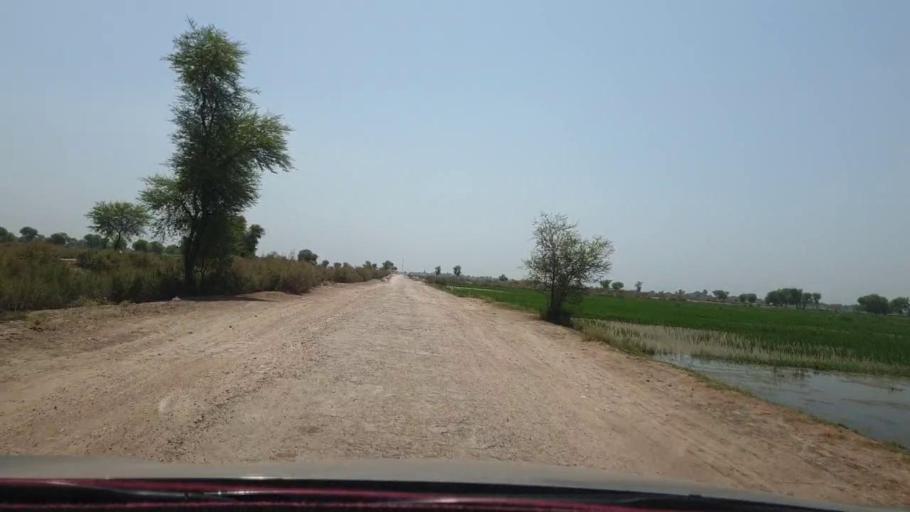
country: PK
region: Sindh
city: Kambar
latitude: 27.5687
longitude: 67.8810
